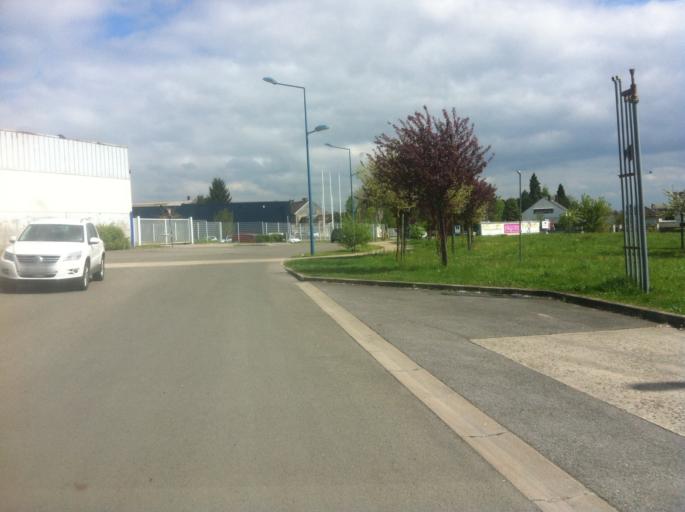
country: FR
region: Picardie
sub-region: Departement de l'Aisne
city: Villers-Cotterets
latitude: 49.2558
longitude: 3.0802
